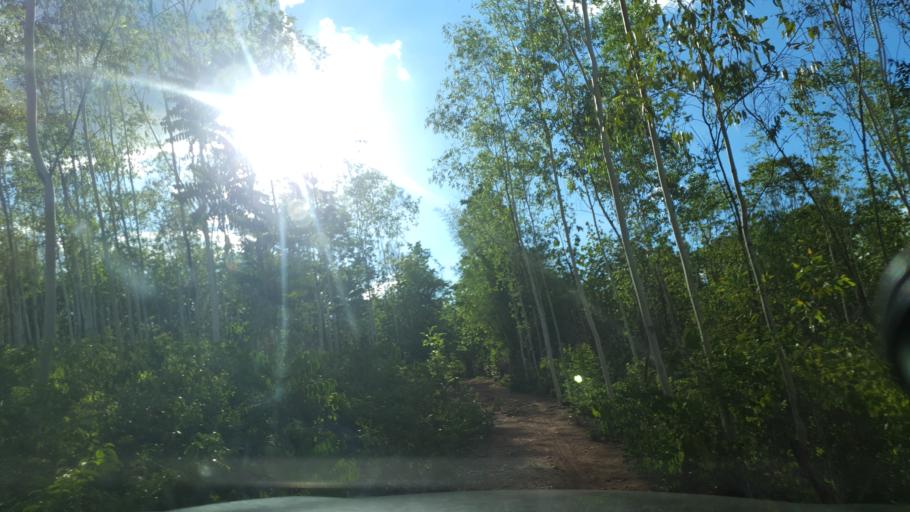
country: TH
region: Lampang
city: Sop Prap
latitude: 17.8930
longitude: 99.2843
